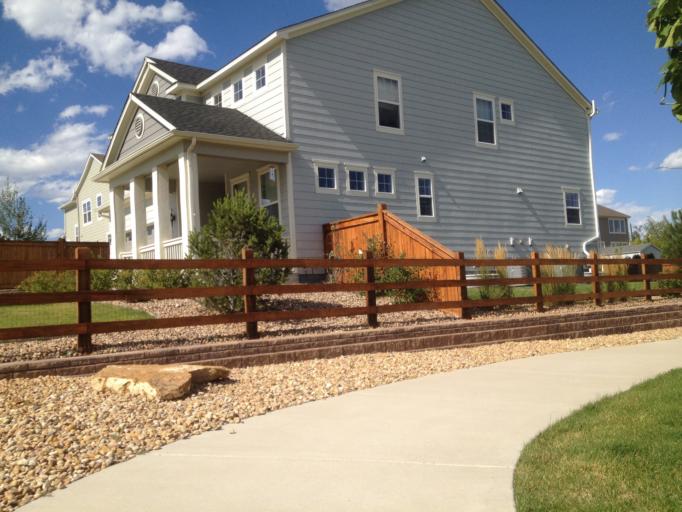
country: US
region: Colorado
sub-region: Boulder County
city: Lafayette
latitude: 40.0042
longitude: -105.0943
